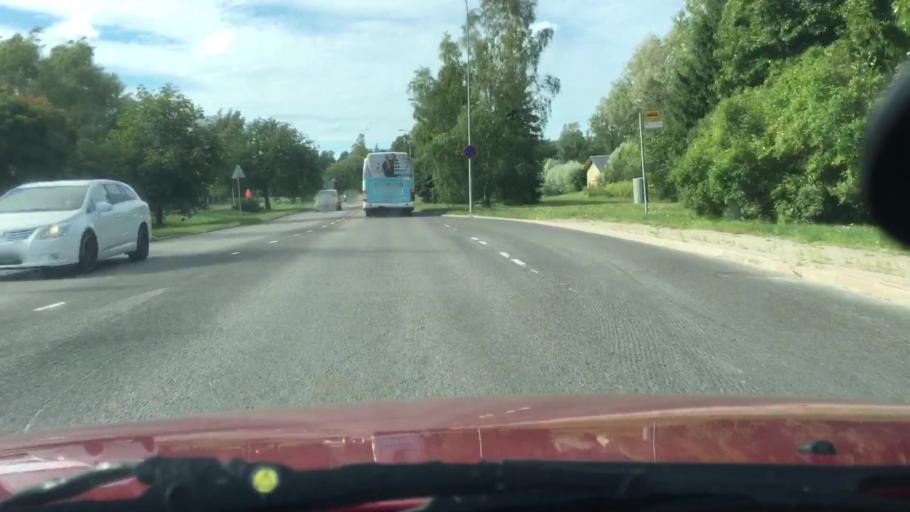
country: FI
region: Varsinais-Suomi
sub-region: Turku
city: Turku
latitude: 60.4611
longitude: 22.2458
